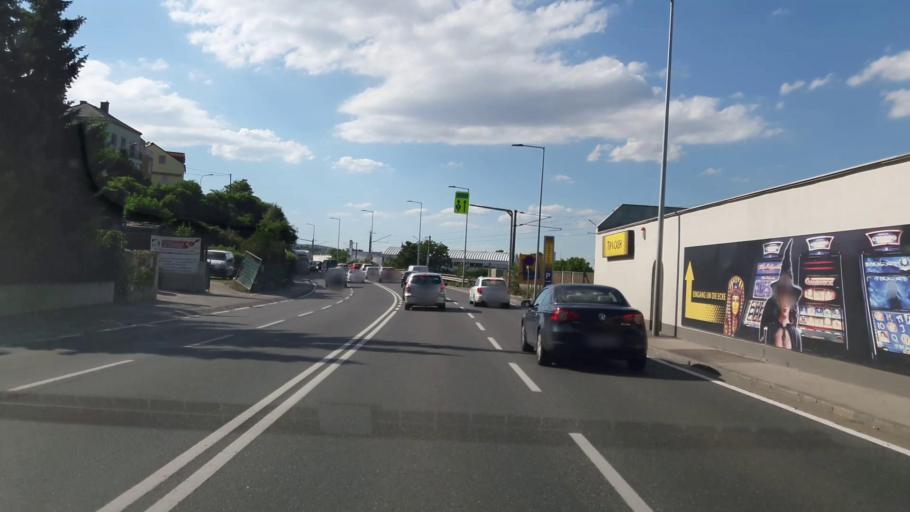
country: AT
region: Lower Austria
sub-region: Politischer Bezirk Korneuburg
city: Langenzersdorf
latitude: 48.2877
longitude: 16.3427
